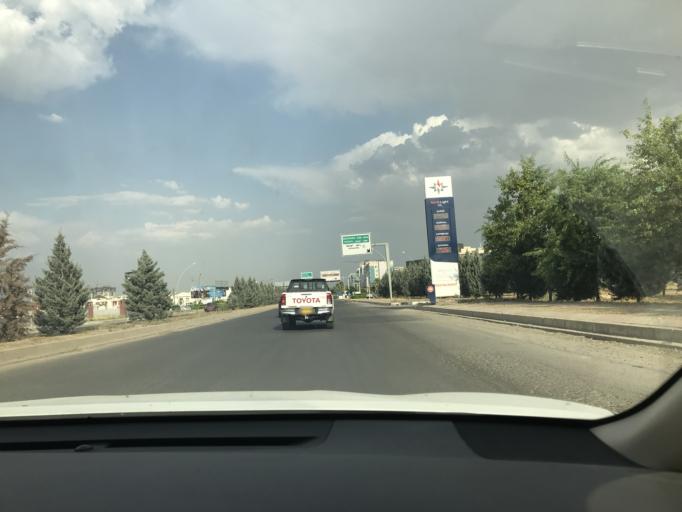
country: IQ
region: Arbil
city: Erbil
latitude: 36.2050
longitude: 43.9651
